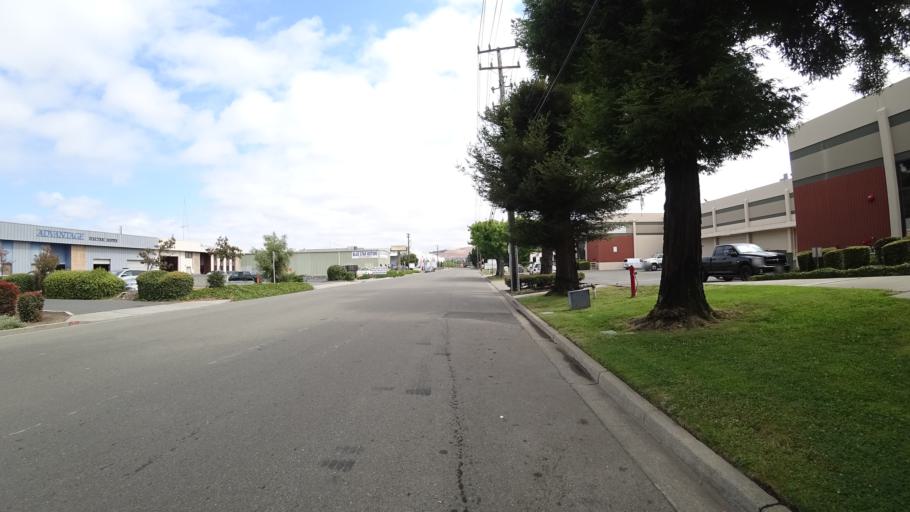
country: US
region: California
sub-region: Alameda County
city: Union City
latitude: 37.6070
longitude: -122.0453
